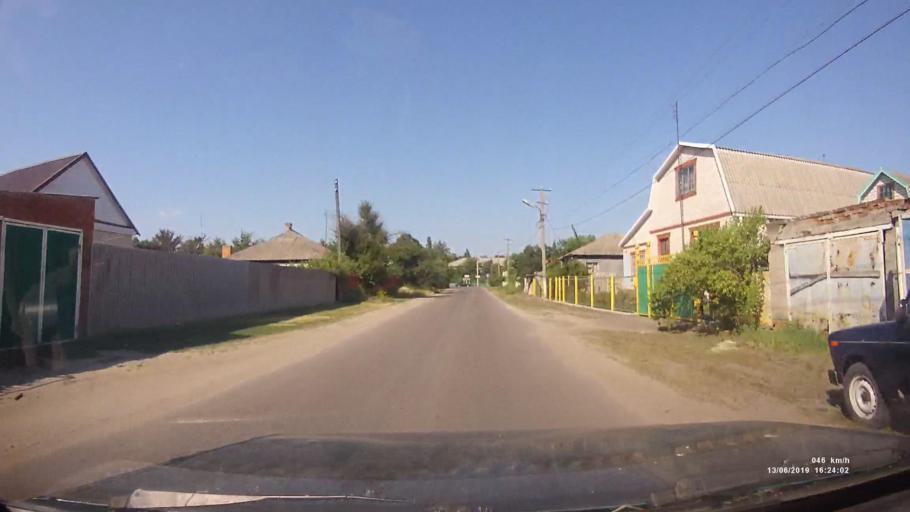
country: RU
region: Rostov
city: Kazanskaya
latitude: 49.7966
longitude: 41.1445
